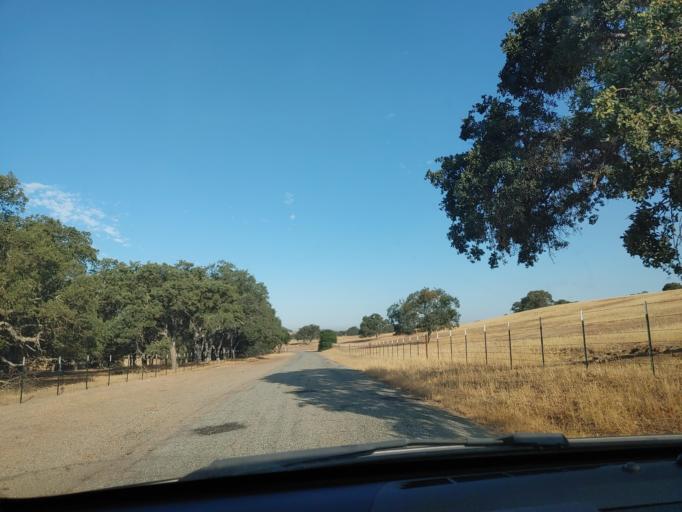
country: US
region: California
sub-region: San Benito County
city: Ridgemark
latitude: 36.7731
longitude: -121.2283
